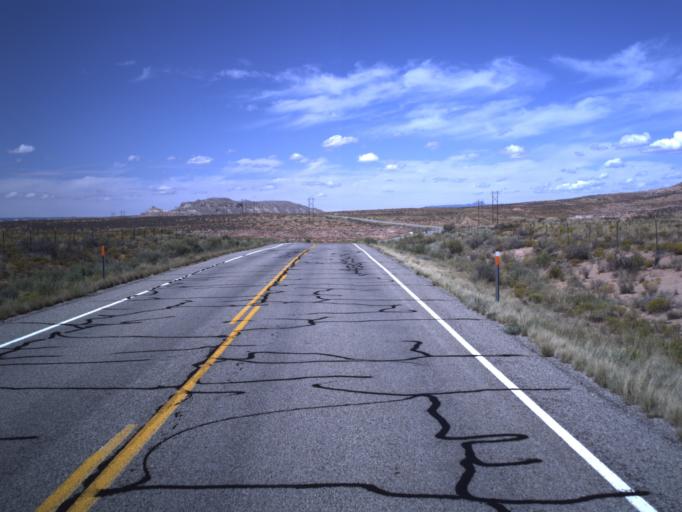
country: US
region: Utah
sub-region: San Juan County
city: Blanding
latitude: 37.2946
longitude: -109.4240
